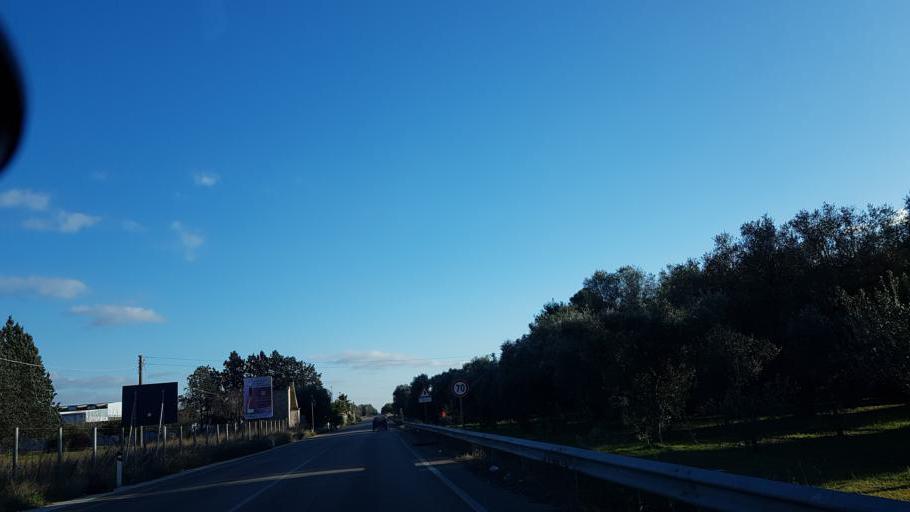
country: IT
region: Apulia
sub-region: Provincia di Brindisi
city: San Pietro Vernotico
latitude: 40.4753
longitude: 18.0092
